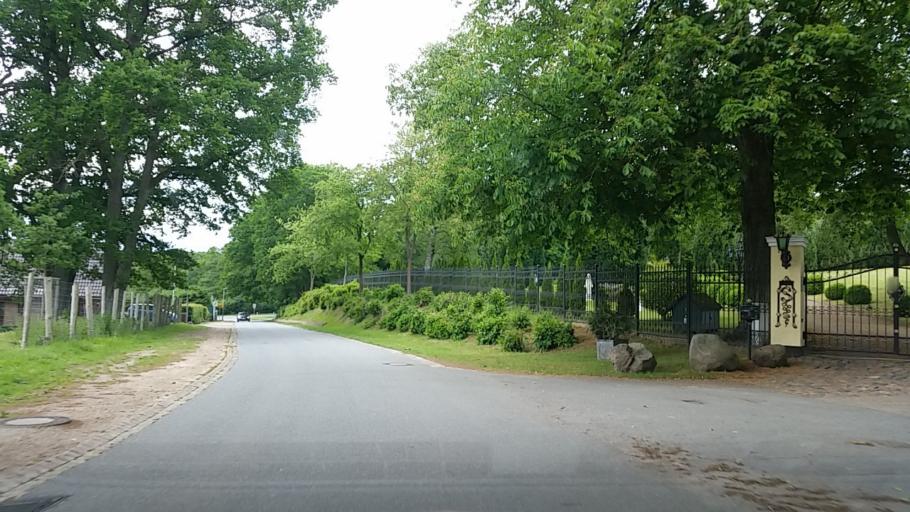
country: DE
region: Schleswig-Holstein
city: Dahmker
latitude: 53.6053
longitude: 10.4429
